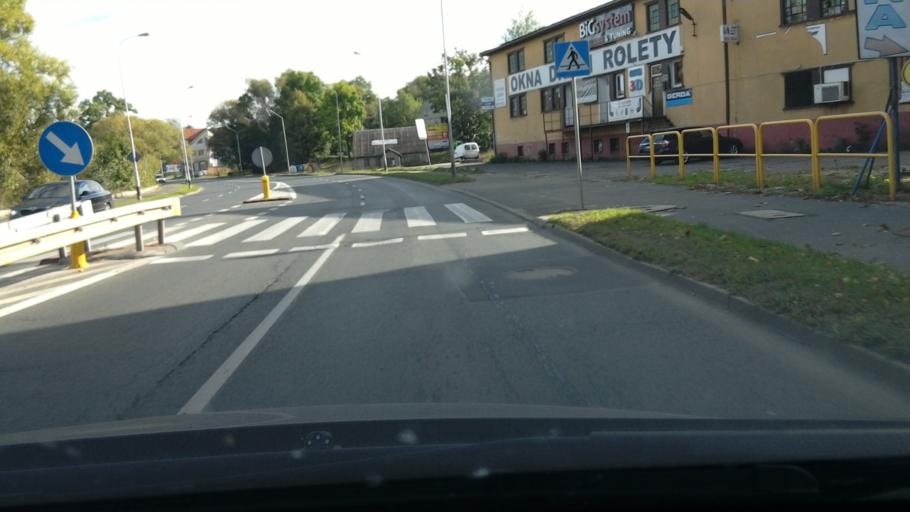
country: PL
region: Lower Silesian Voivodeship
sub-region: Jelenia Gora
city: Cieplice Slaskie Zdroj
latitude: 50.8783
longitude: 15.7076
